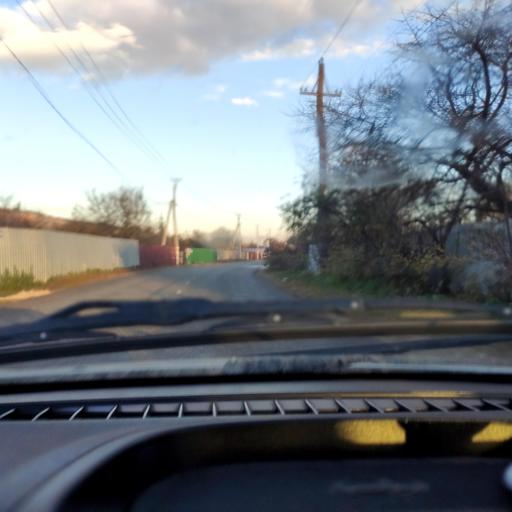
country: RU
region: Samara
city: Zhigulevsk
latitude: 53.4661
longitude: 49.6420
